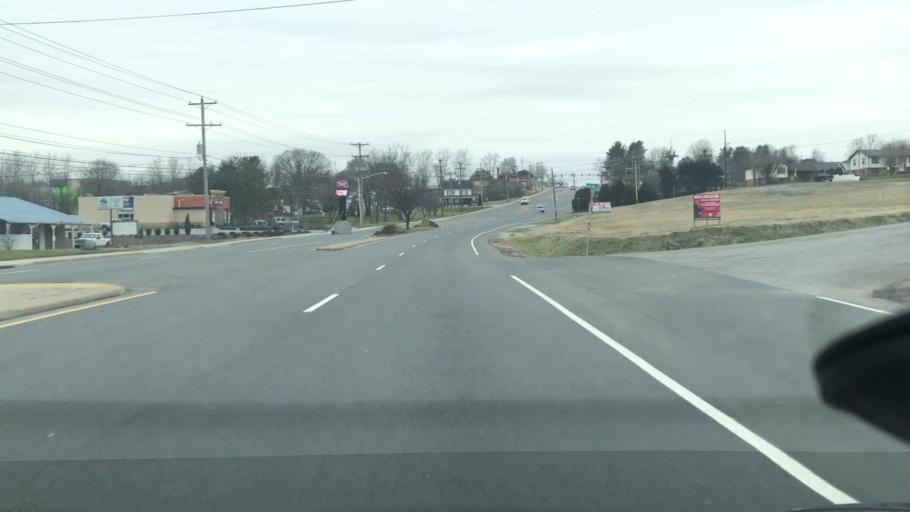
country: US
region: Virginia
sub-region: Montgomery County
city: Christiansburg
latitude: 37.1406
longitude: -80.4148
